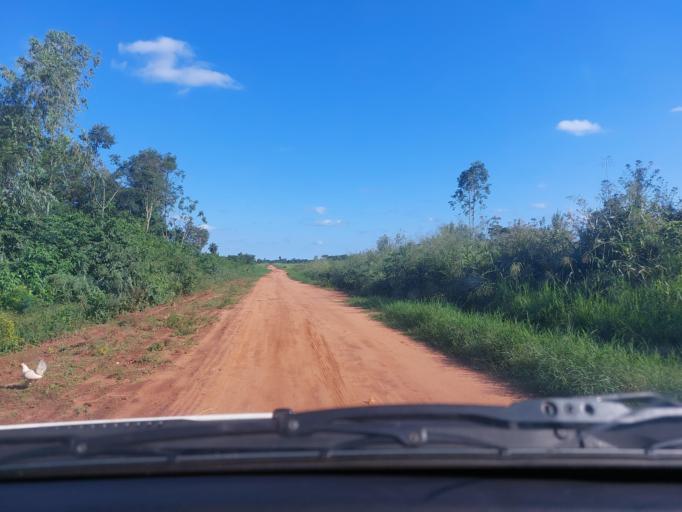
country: PY
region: San Pedro
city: Guayaybi
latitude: -24.5139
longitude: -56.5462
